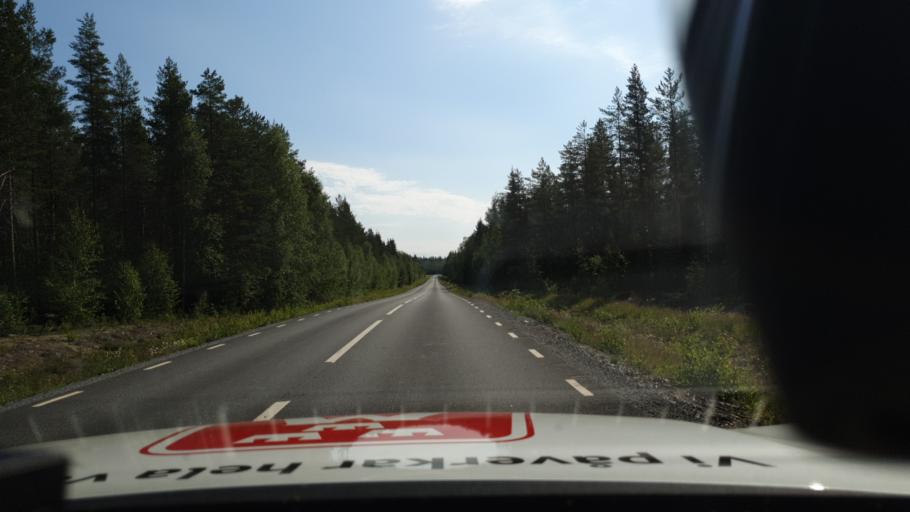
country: SE
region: Norrbotten
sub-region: Bodens Kommun
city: Boden
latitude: 65.8446
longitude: 21.7695
